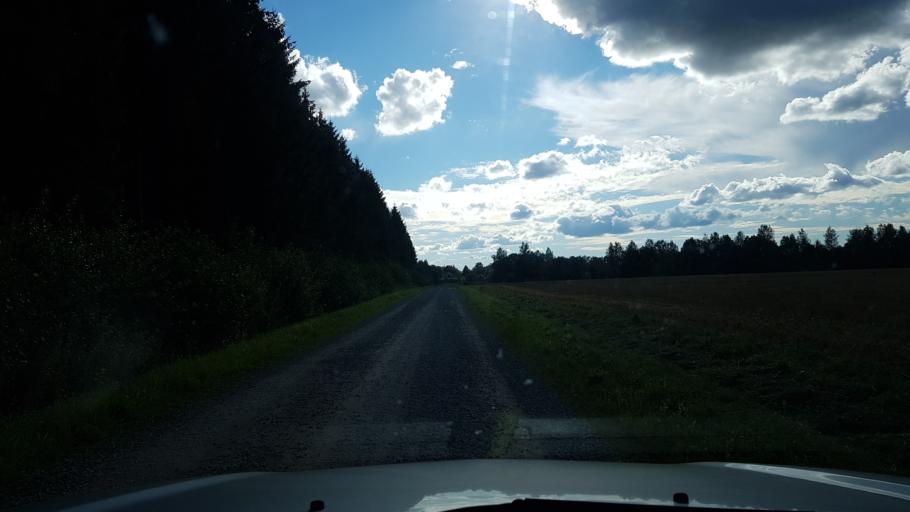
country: EE
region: Harju
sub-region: Rae vald
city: Jueri
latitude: 59.3514
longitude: 24.8563
